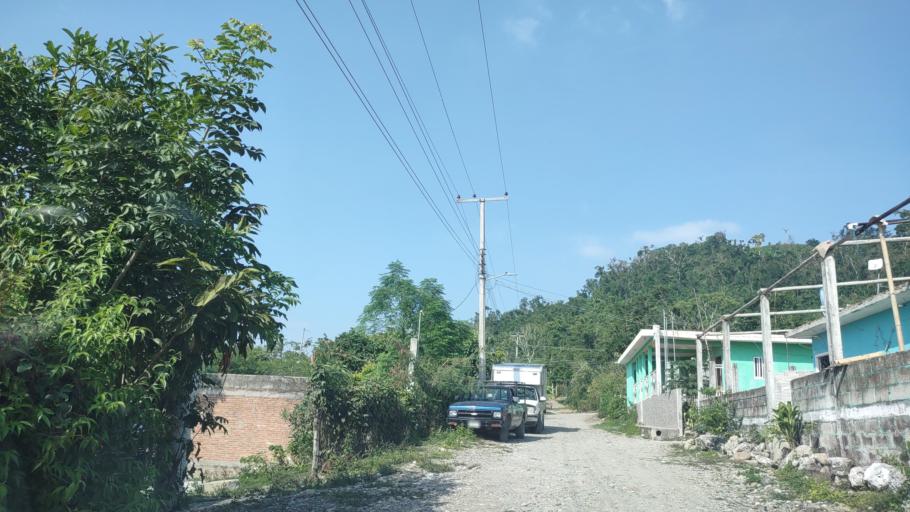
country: MX
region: Veracruz
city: Agua Dulce
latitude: 20.2957
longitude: -97.2808
